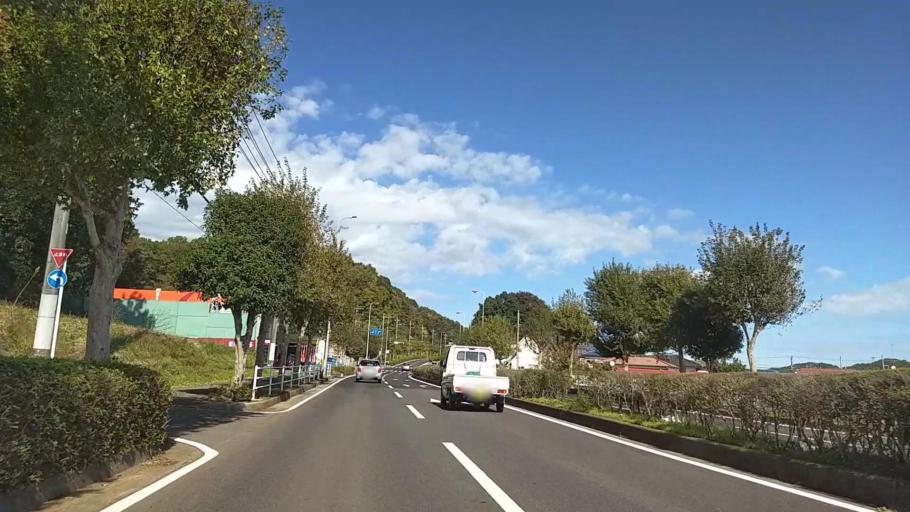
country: JP
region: Kanagawa
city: Hadano
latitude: 35.3420
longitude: 139.2303
